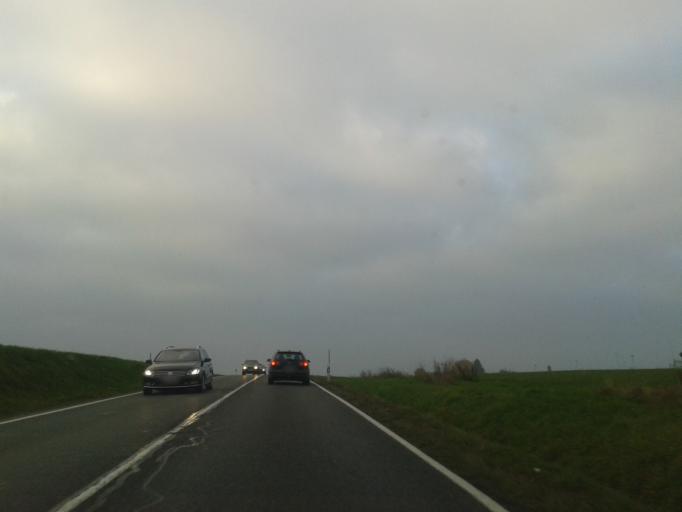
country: DE
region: Saxony
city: Niederschona
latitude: 50.9598
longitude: 13.4217
